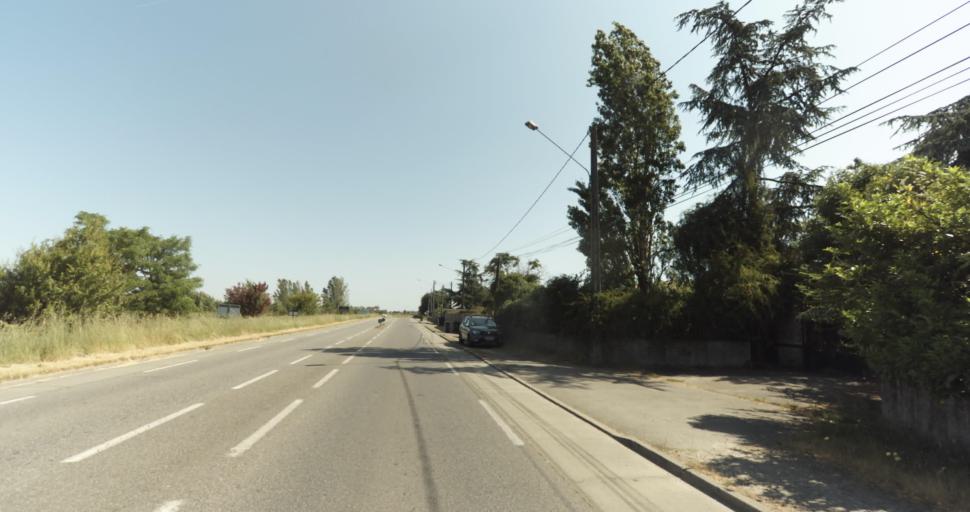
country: FR
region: Midi-Pyrenees
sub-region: Departement de la Haute-Garonne
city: La Salvetat-Saint-Gilles
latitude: 43.5844
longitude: 1.2787
